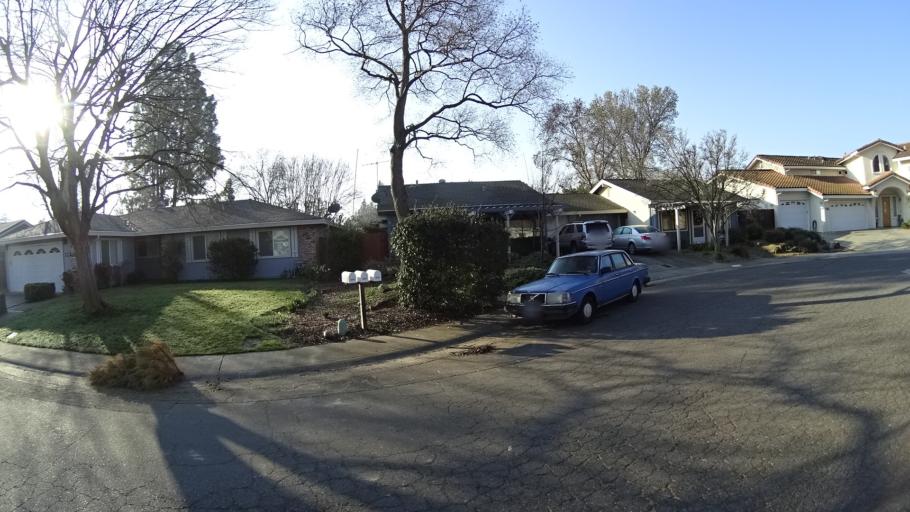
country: US
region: California
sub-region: Yolo County
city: Davis
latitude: 38.5568
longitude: -121.7931
